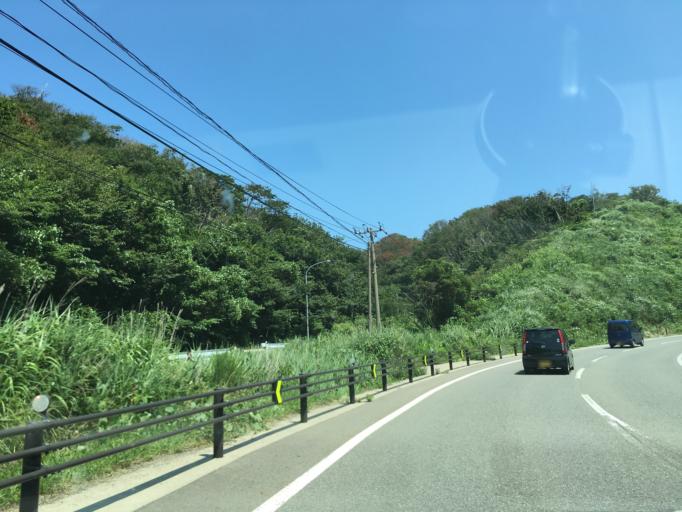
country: JP
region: Akita
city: Tenno
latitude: 39.9598
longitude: 139.7184
